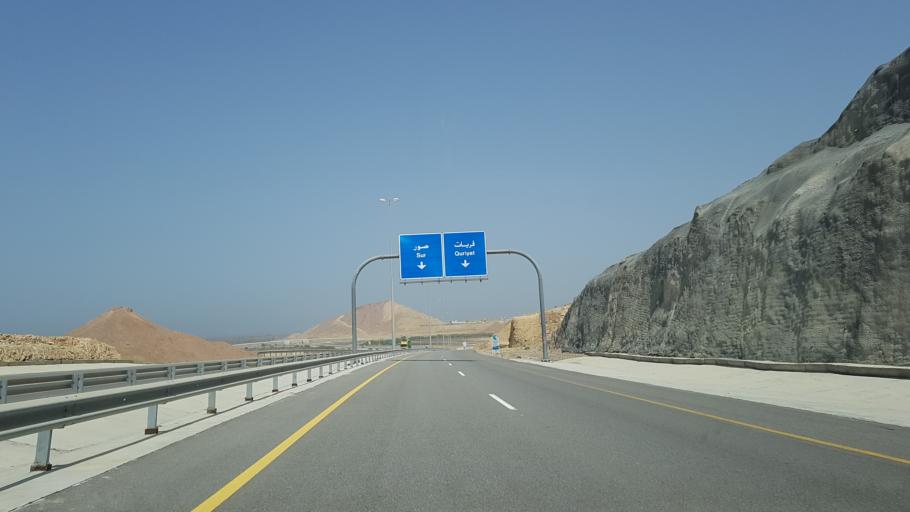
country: OM
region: Muhafazat Masqat
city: Muscat
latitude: 23.2062
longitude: 58.9105
